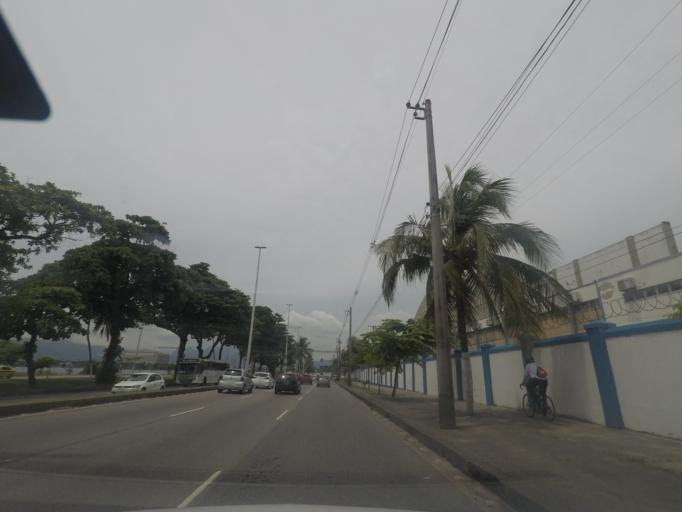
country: BR
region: Rio de Janeiro
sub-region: Rio De Janeiro
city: Rio de Janeiro
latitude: -22.8271
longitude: -43.2344
